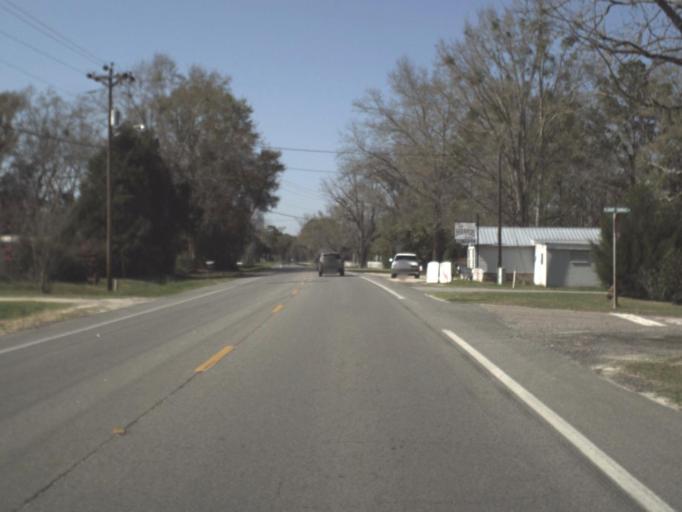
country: US
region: Florida
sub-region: Gulf County
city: Wewahitchka
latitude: 30.0950
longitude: -85.1971
